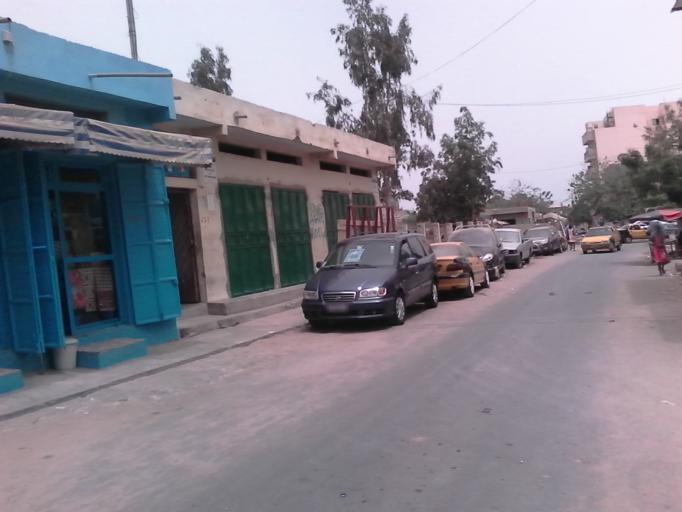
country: SN
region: Dakar
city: Grand Dakar
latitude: 14.7045
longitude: -17.4540
